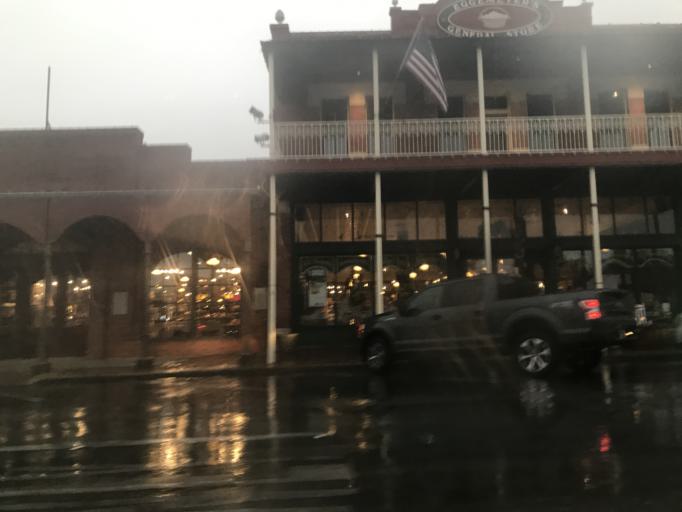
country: US
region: Texas
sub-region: Tom Green County
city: San Angelo
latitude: 31.4604
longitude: -100.4342
